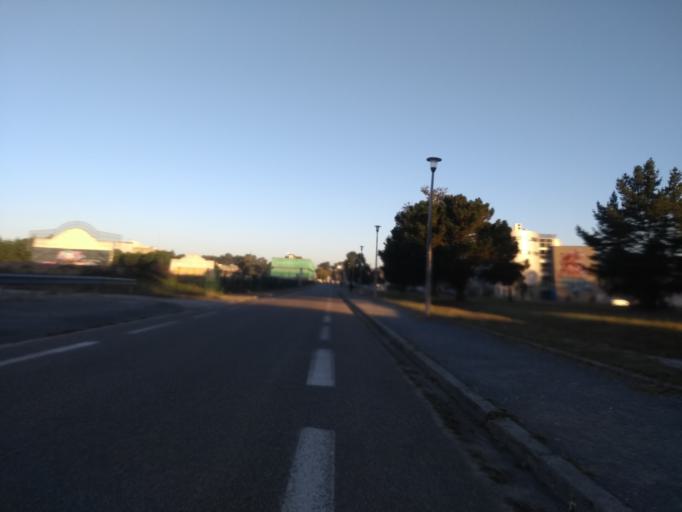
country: FR
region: Aquitaine
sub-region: Departement de la Gironde
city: Gradignan
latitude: 44.7921
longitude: -0.6145
